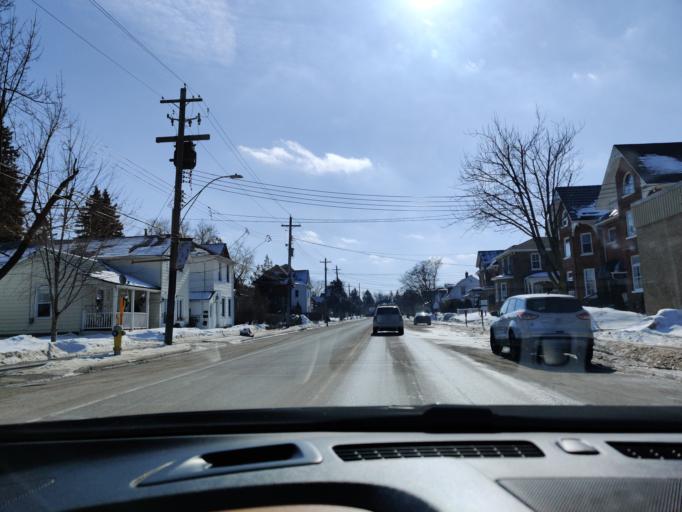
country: CA
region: Ontario
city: Collingwood
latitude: 44.4983
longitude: -80.2149
